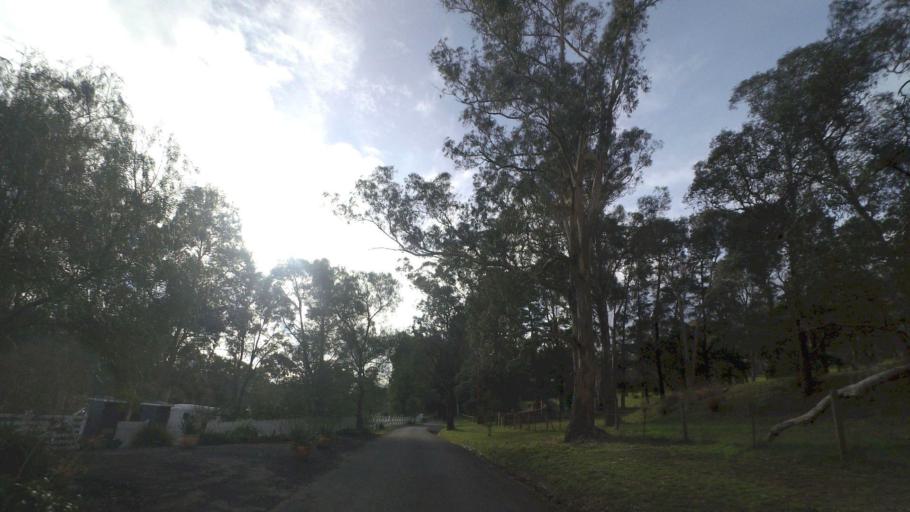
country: AU
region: Victoria
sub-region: Manningham
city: Warrandyte
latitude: -37.7381
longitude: 145.2320
